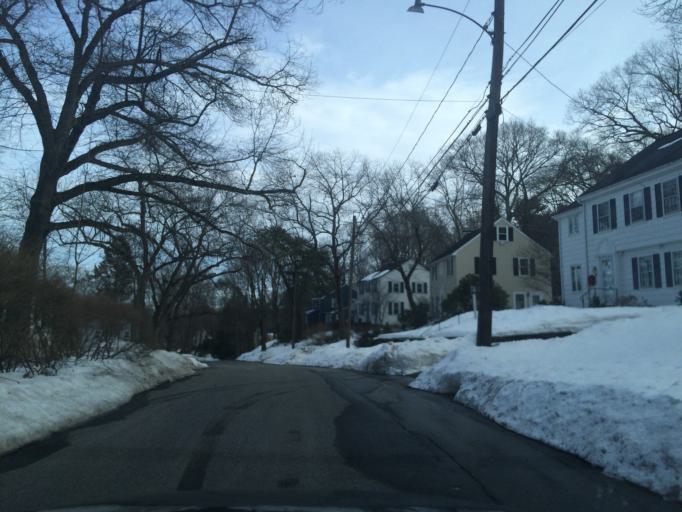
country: US
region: Massachusetts
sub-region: Middlesex County
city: Lexington
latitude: 42.4320
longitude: -71.2112
